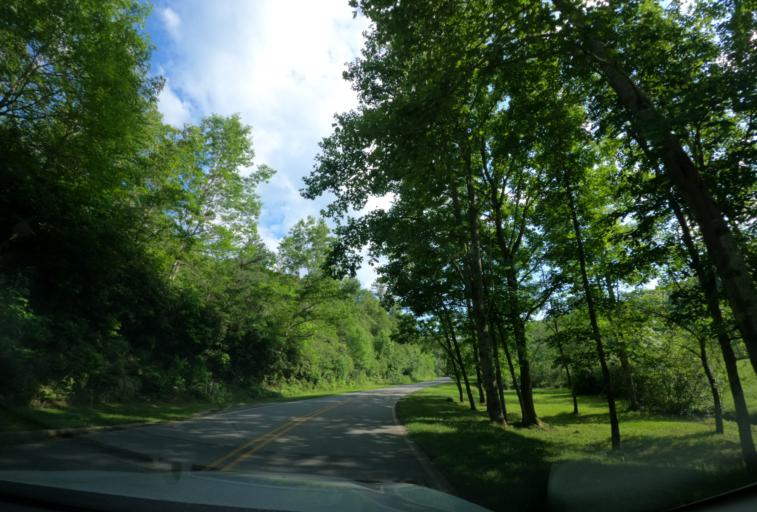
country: US
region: North Carolina
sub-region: Transylvania County
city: Brevard
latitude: 35.2413
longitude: -82.8592
